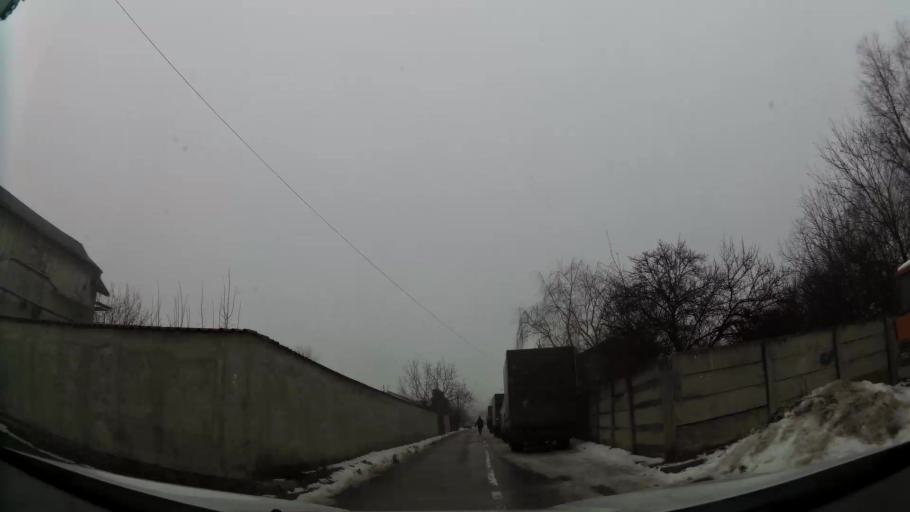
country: RO
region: Ilfov
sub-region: Comuna Chiajna
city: Rosu
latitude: 44.4444
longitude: 26.0151
